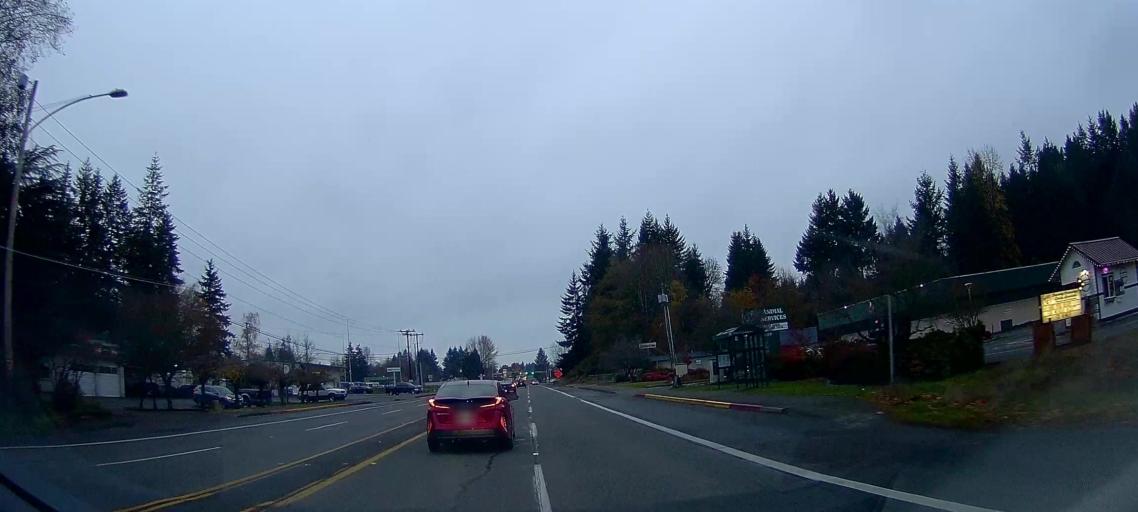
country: US
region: Washington
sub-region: Thurston County
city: Lacey
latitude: 47.0466
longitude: -122.8545
